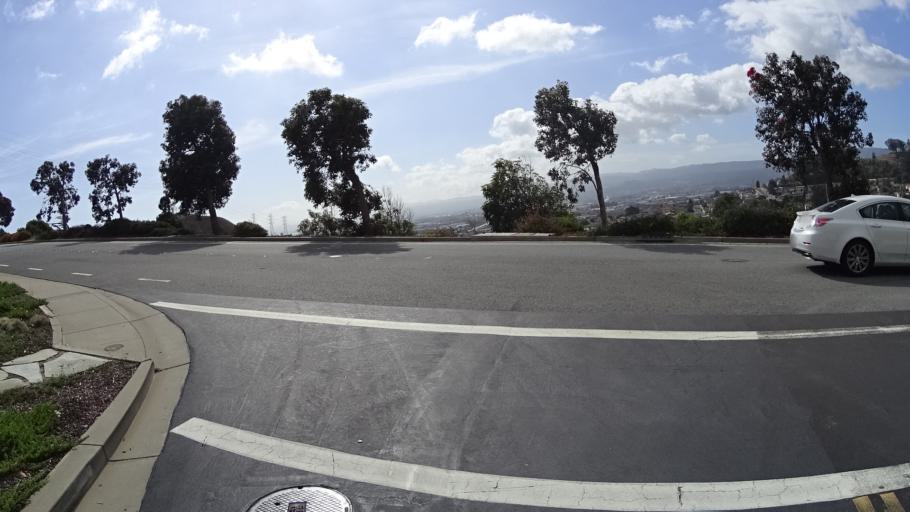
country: US
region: California
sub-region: San Mateo County
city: South San Francisco
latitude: 37.6672
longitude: -122.4082
